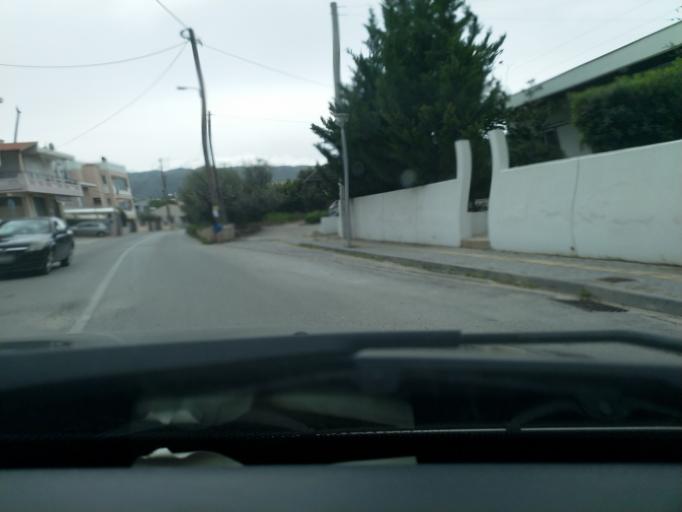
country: GR
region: Crete
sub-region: Nomos Chanias
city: Chania
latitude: 35.4989
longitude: 24.0215
